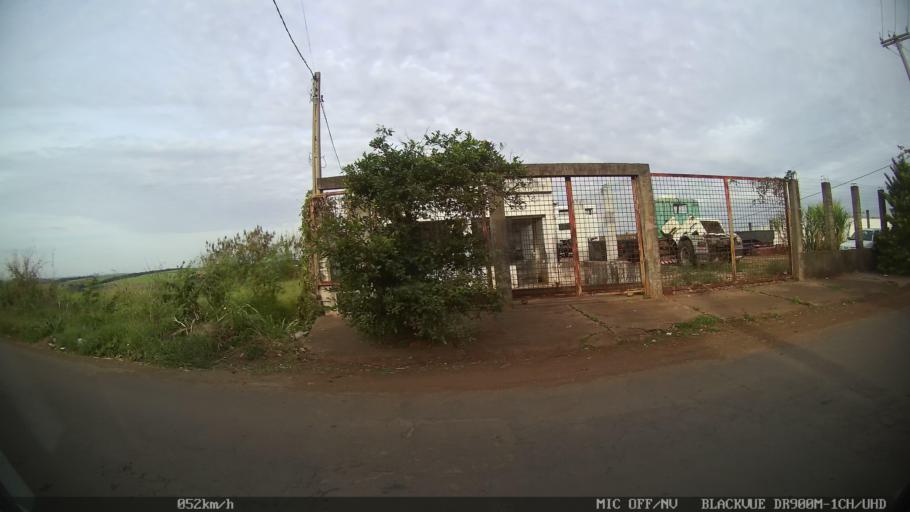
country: BR
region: Sao Paulo
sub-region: Piracicaba
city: Piracicaba
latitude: -22.7317
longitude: -47.5875
